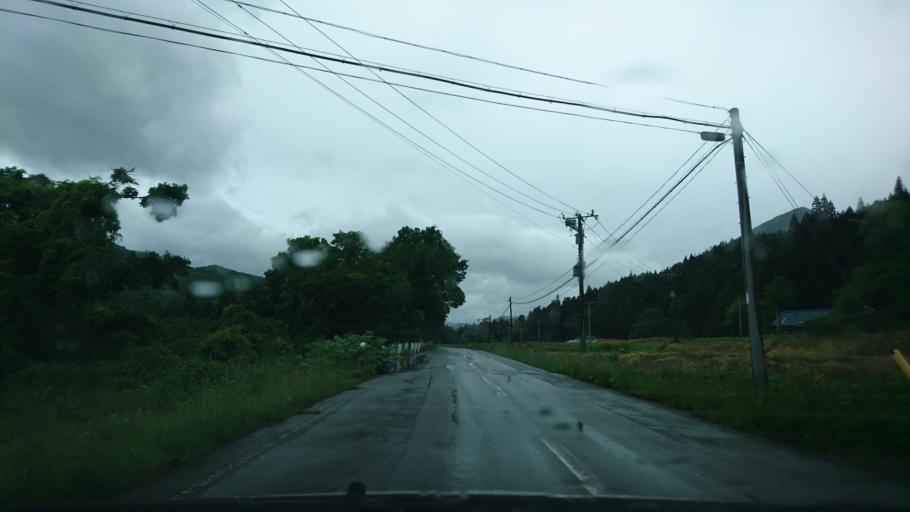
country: JP
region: Iwate
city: Ichinoseki
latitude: 38.9919
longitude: 140.9048
